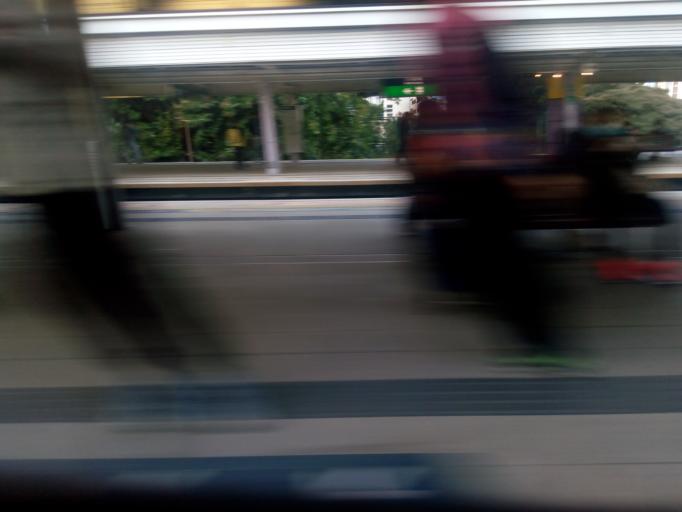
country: HK
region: Tai Po
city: Tai Po
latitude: 22.4447
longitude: 114.1712
